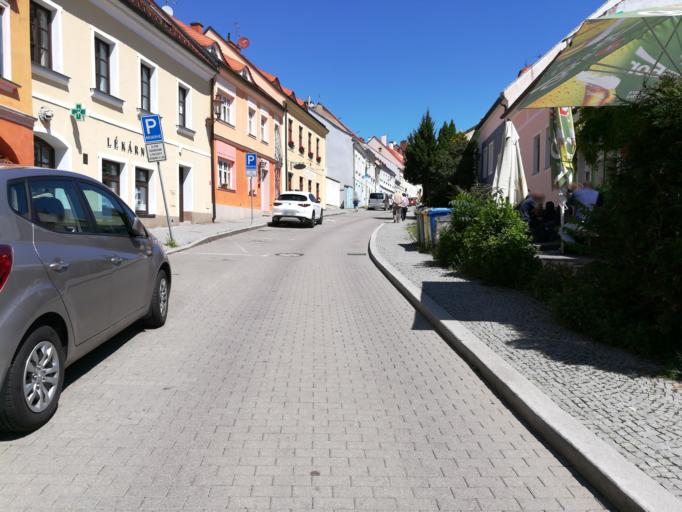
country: CZ
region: South Moravian
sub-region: Okres Breclav
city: Mikulov
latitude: 48.8052
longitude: 16.6348
